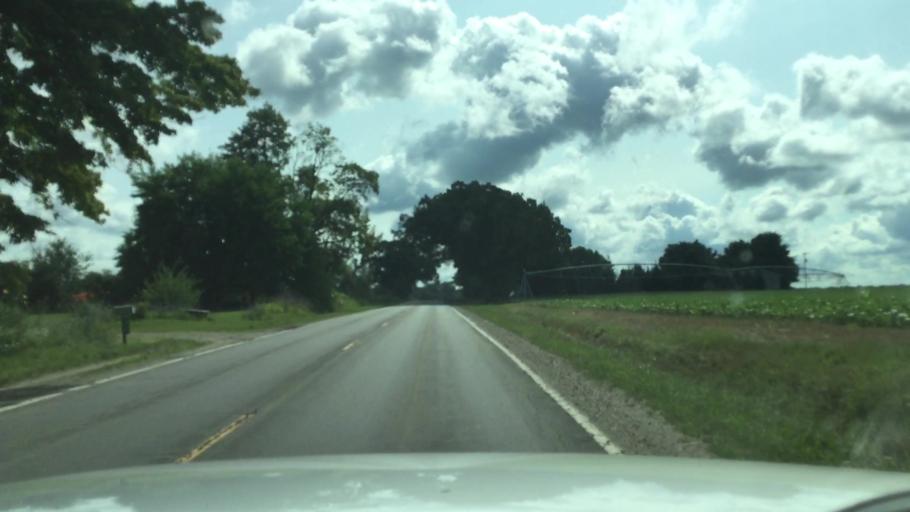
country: US
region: Michigan
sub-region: Montcalm County
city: Greenville
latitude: 43.1922
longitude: -85.2019
